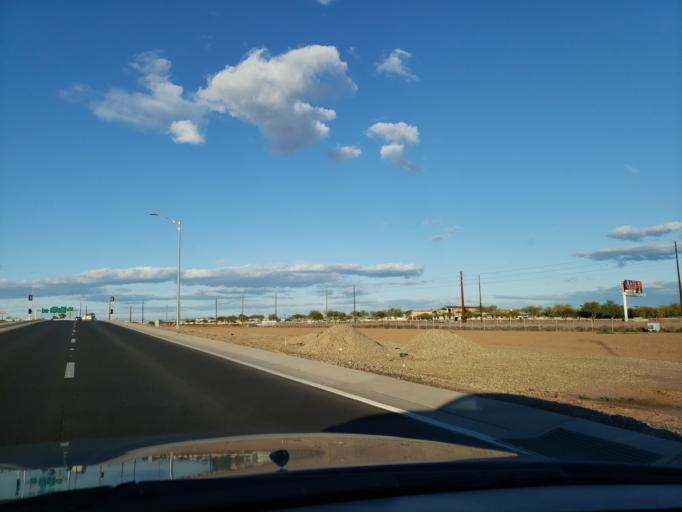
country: US
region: Arizona
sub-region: Maricopa County
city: Laveen
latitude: 33.4239
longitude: -112.1884
